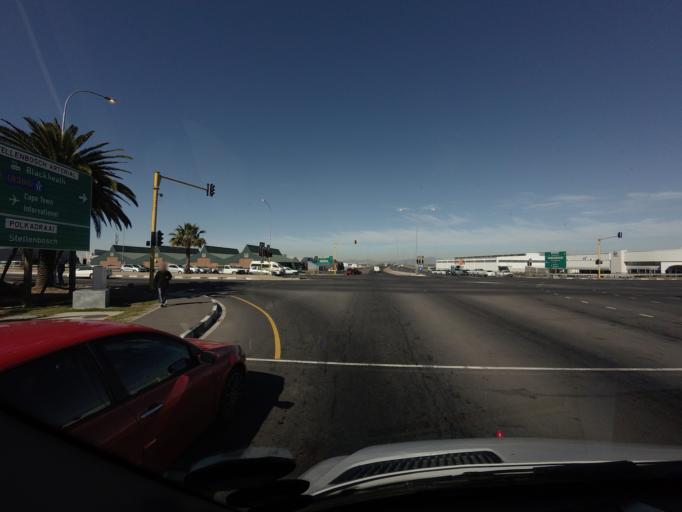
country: ZA
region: Western Cape
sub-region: City of Cape Town
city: Kraaifontein
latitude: -33.9515
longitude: 18.6961
